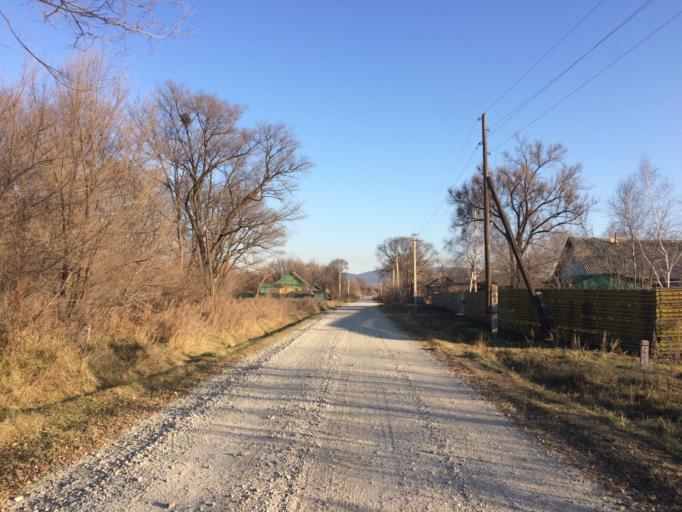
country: RU
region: Primorskiy
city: Ivanovka
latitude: 43.9569
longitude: 132.4794
